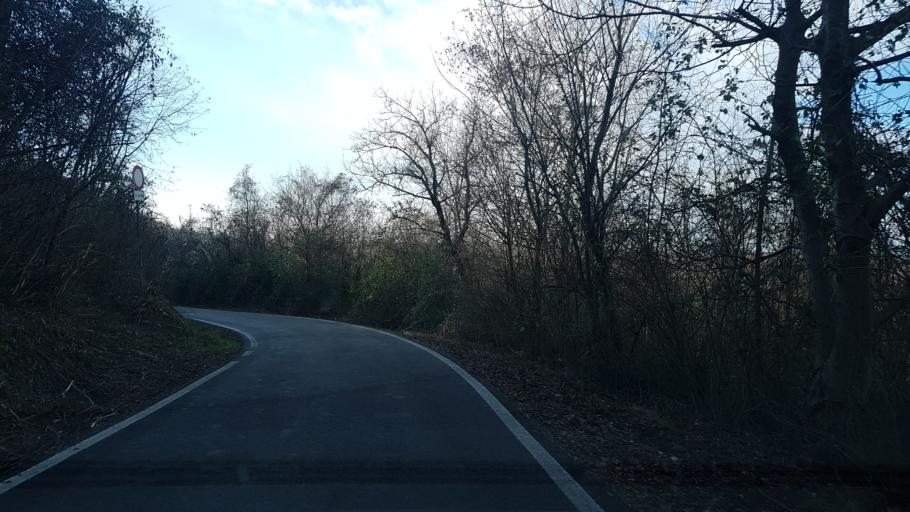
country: IT
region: Friuli Venezia Giulia
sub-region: Provincia di Gorizia
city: Farra d'Isonzo
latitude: 45.8938
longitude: 13.5433
